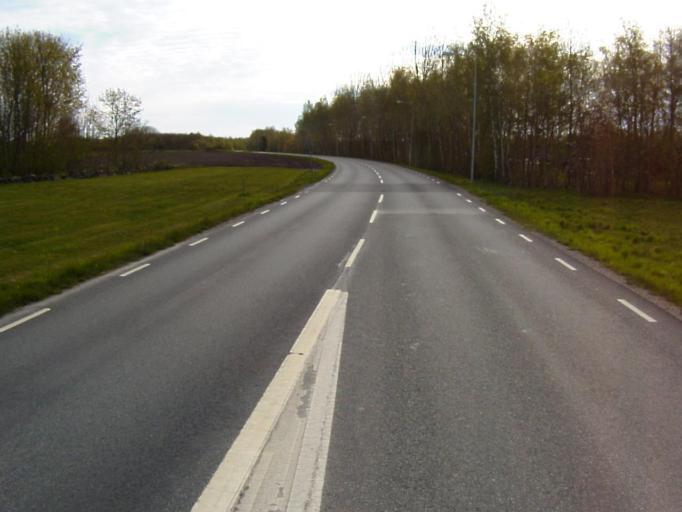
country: SE
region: Skane
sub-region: Kristianstads Kommun
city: Norra Asum
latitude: 56.0026
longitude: 14.1404
